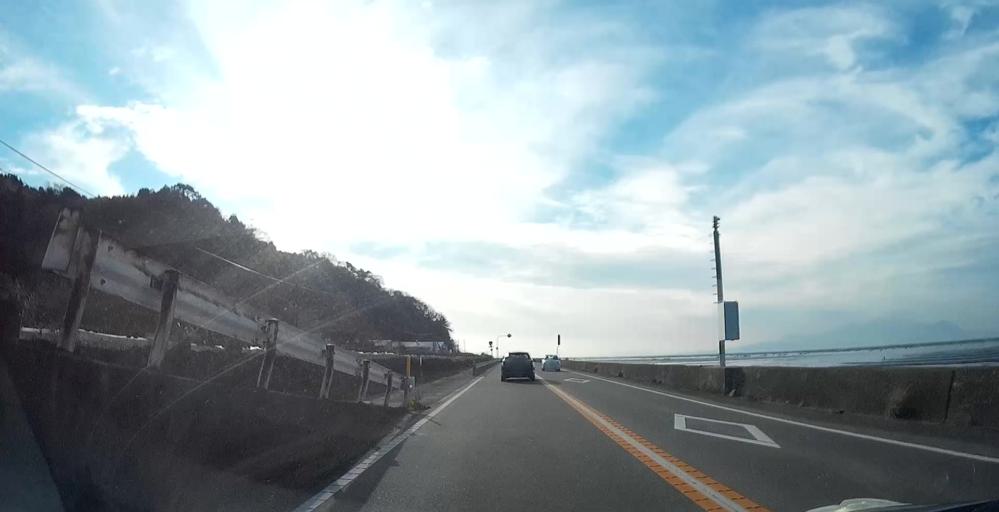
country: JP
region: Kumamoto
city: Uto
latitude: 32.7000
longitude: 130.5701
